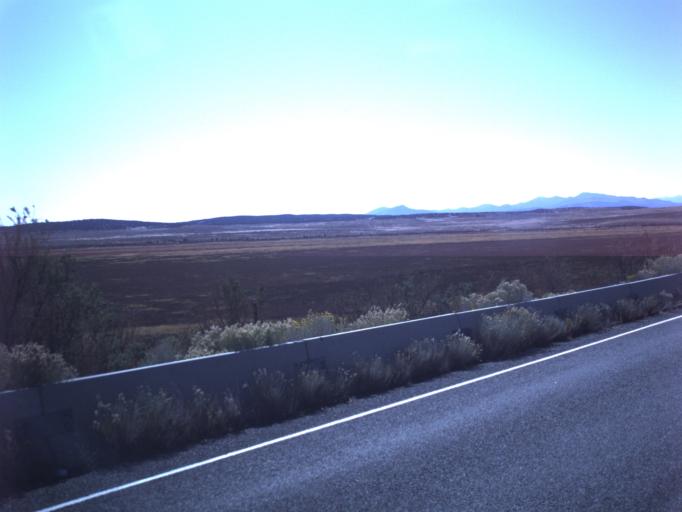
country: US
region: Utah
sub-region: Juab County
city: Nephi
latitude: 39.4940
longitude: -111.9643
